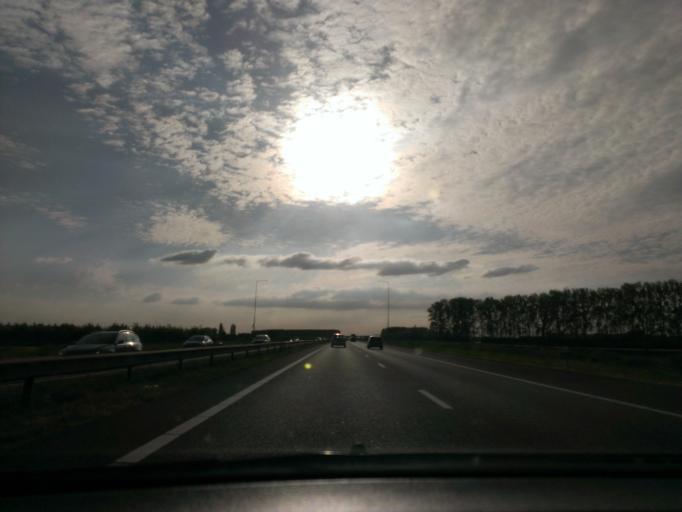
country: NL
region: Gelderland
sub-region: Gemeente Overbetuwe
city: Zetten
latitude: 51.9174
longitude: 5.6867
